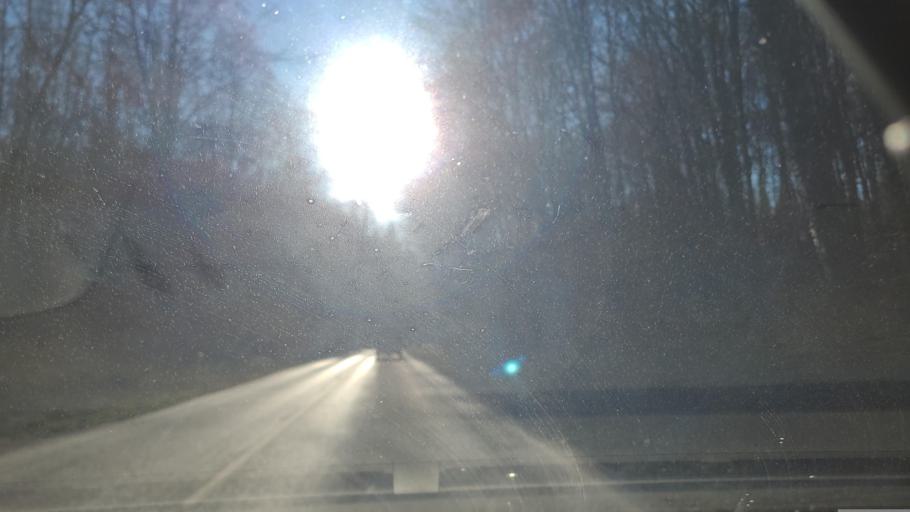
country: LU
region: Luxembourg
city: Bridel
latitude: 49.6380
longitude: 6.0856
